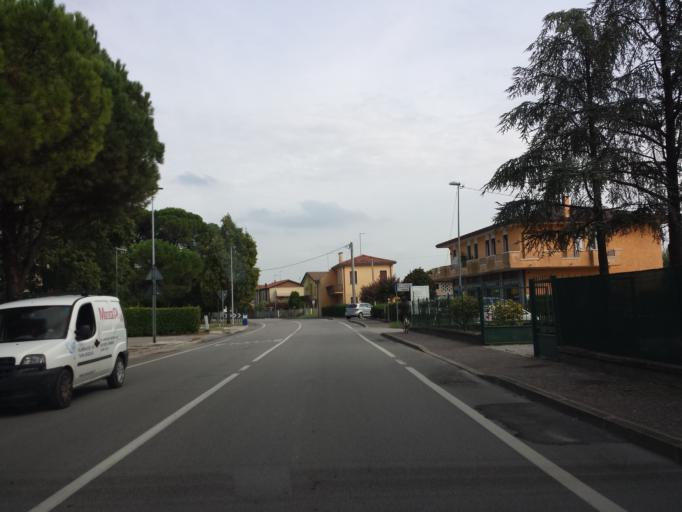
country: IT
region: Veneto
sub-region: Provincia di Padova
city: Codiverno
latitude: 45.4955
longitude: 11.9424
